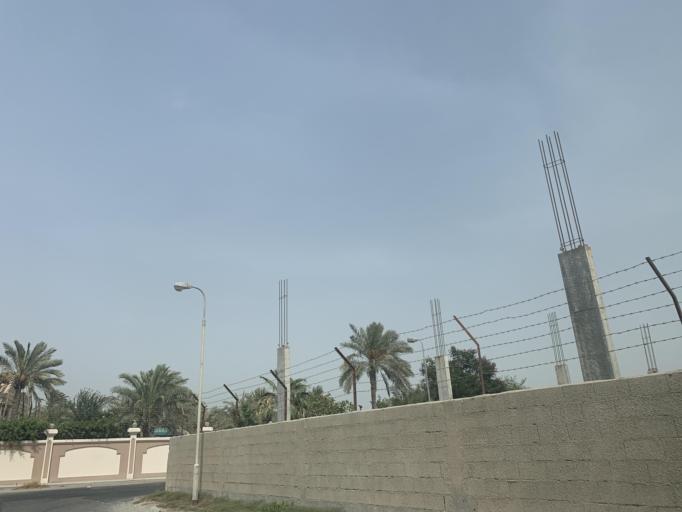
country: BH
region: Manama
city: Jidd Hafs
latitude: 26.1993
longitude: 50.4759
